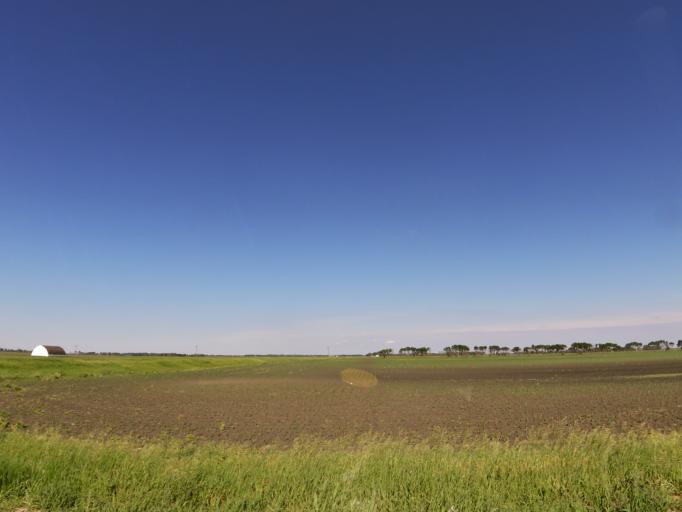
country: US
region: North Dakota
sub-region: Walsh County
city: Grafton
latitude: 48.3974
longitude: -97.2777
